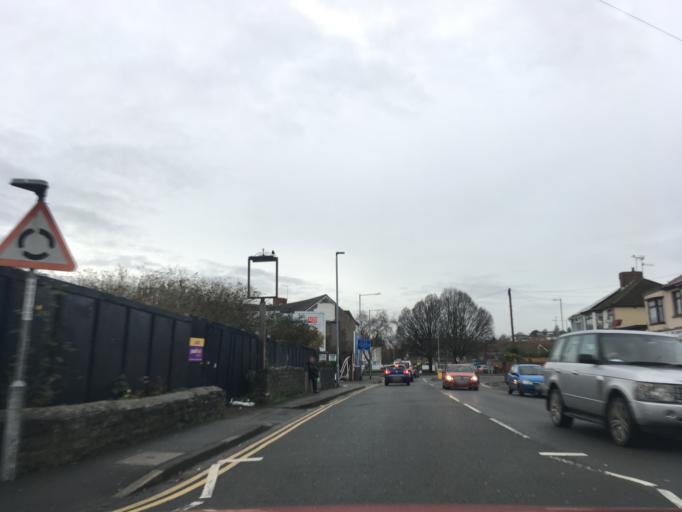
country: GB
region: Wales
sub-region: Newport
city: Caerleon
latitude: 51.5823
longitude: -2.9622
